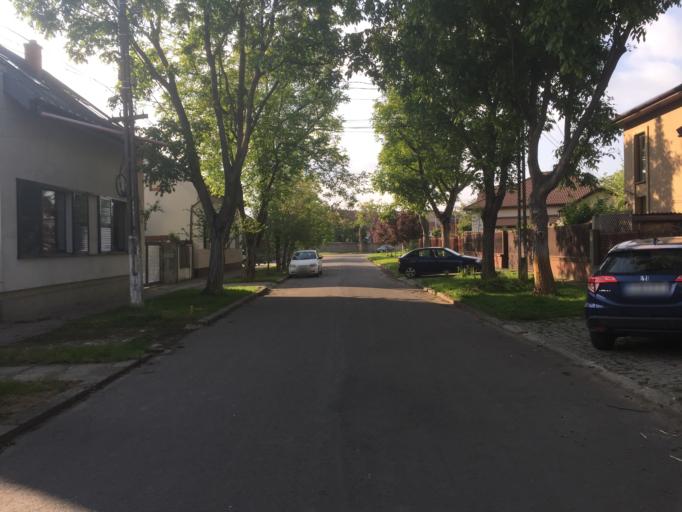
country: RO
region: Timis
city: Timisoara
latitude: 45.7559
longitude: 21.2001
